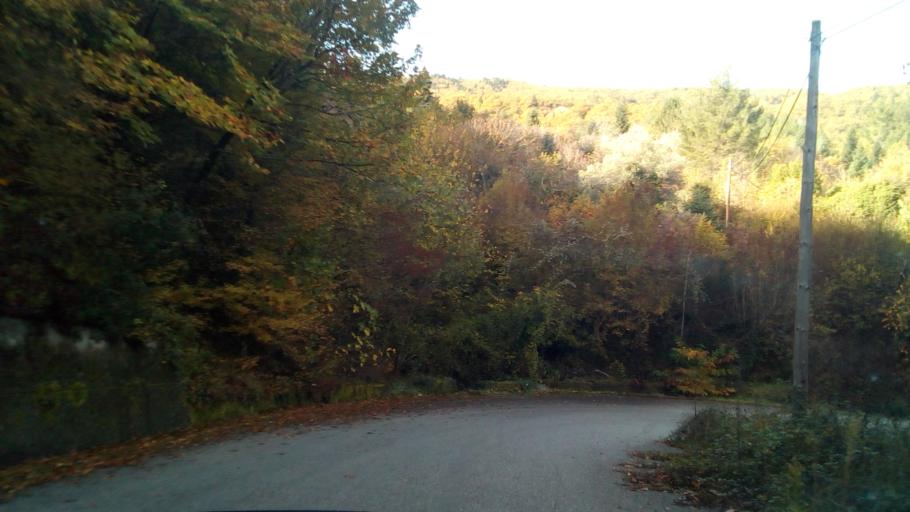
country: GR
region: West Greece
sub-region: Nomos Aitolias kai Akarnanias
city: Thermo
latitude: 38.6576
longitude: 21.8405
